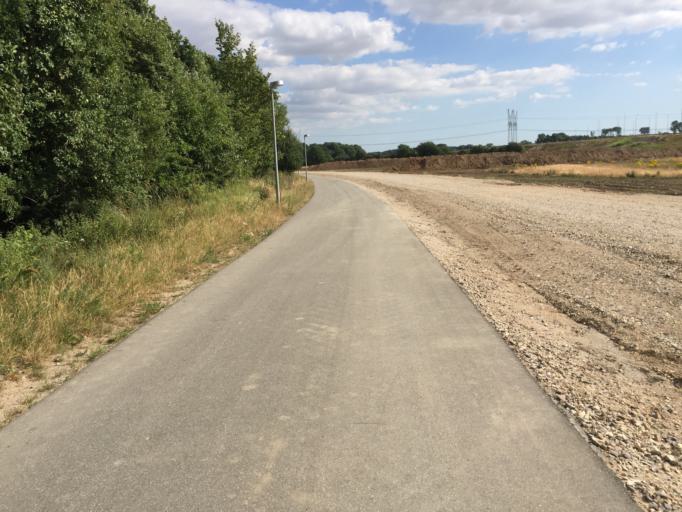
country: DK
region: South Denmark
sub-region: Odense Kommune
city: Hojby
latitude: 55.3538
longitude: 10.4243
